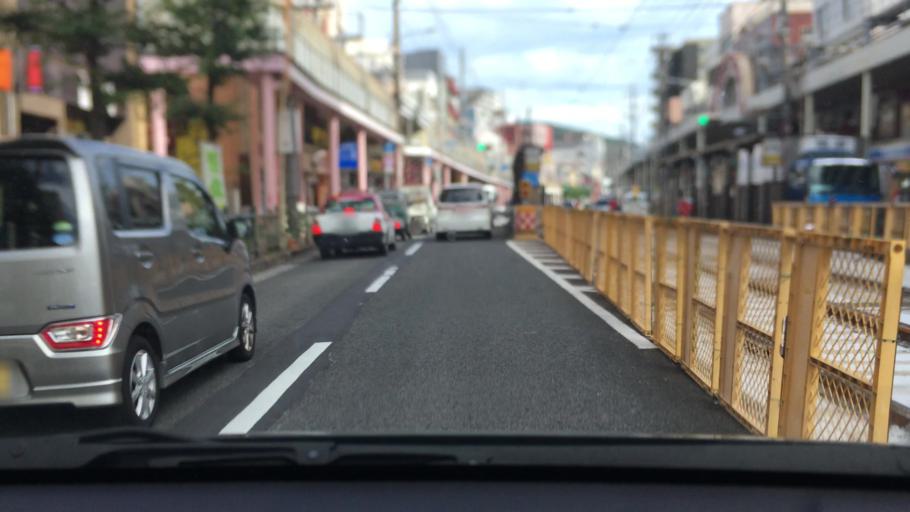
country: JP
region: Nagasaki
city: Obita
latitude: 32.7924
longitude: 129.8596
